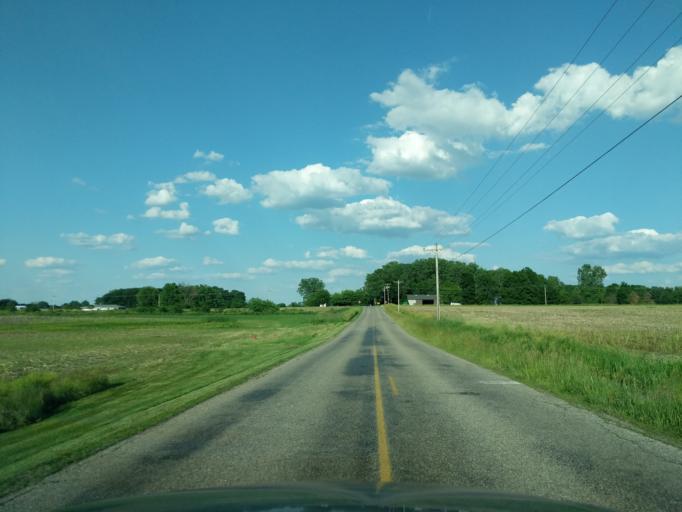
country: US
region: Indiana
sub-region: Whitley County
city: Tri-Lakes
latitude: 41.3026
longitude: -85.5033
